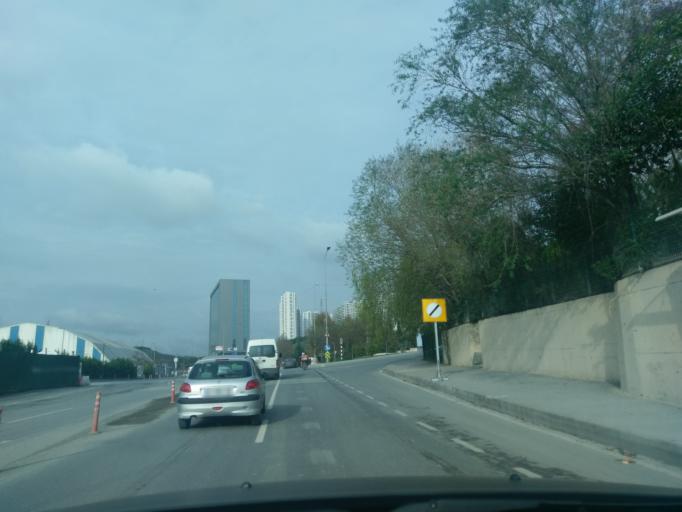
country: TR
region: Istanbul
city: Basaksehir
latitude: 41.0564
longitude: 28.7748
